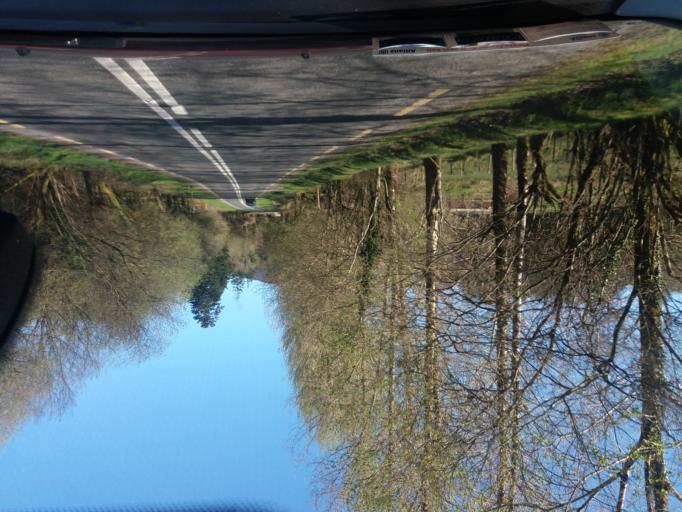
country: IE
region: Munster
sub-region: Ciarrai
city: Cill Airne
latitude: 52.0233
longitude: -9.4914
